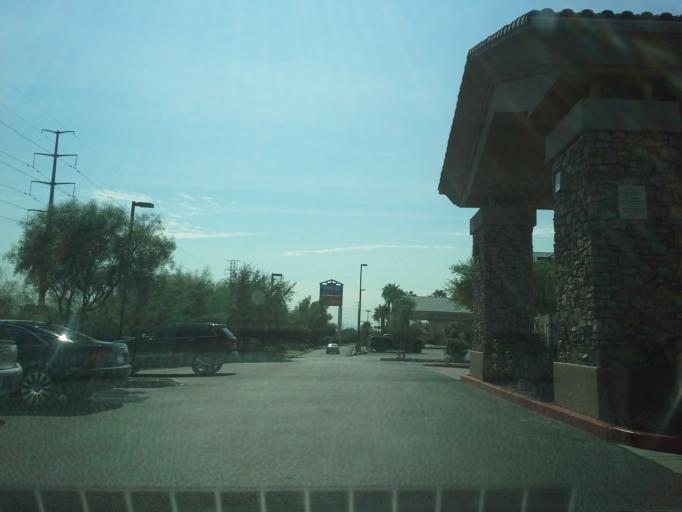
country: US
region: Arizona
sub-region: Pima County
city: Flowing Wells
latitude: 32.2530
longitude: -110.9991
